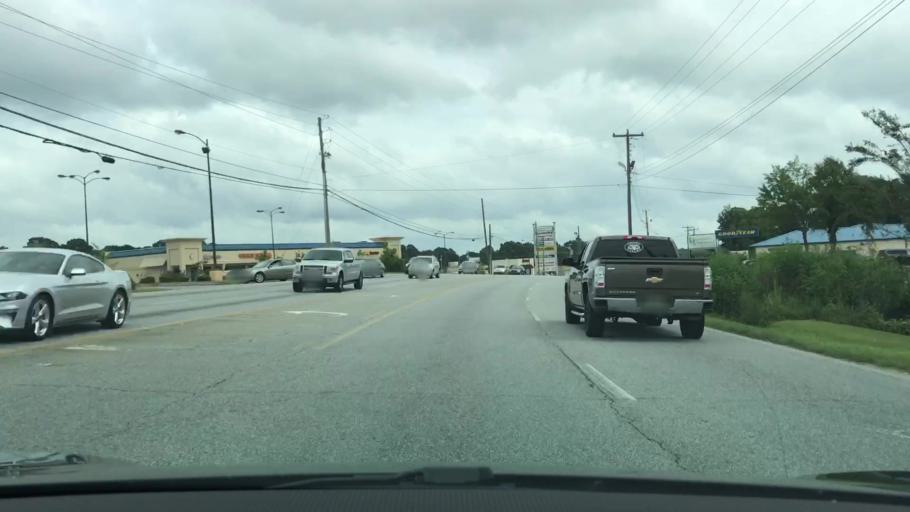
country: US
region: Alabama
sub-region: Lee County
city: Auburn
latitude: 32.6319
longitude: -85.4356
